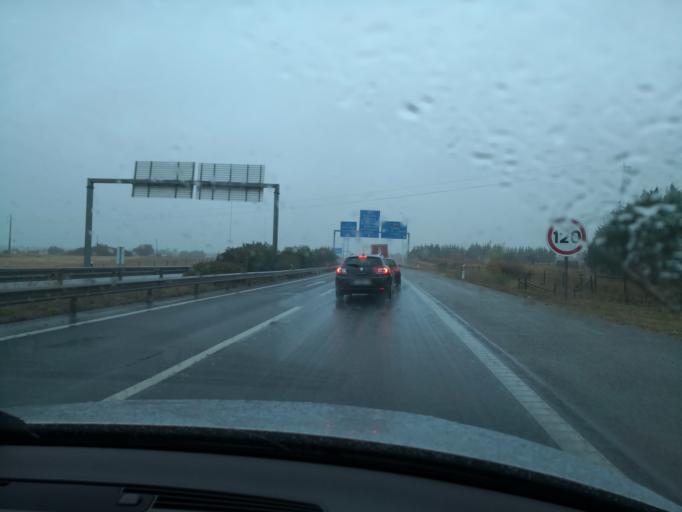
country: PT
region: Setubal
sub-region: Montijo
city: Montijo
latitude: 38.7072
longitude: -8.9394
